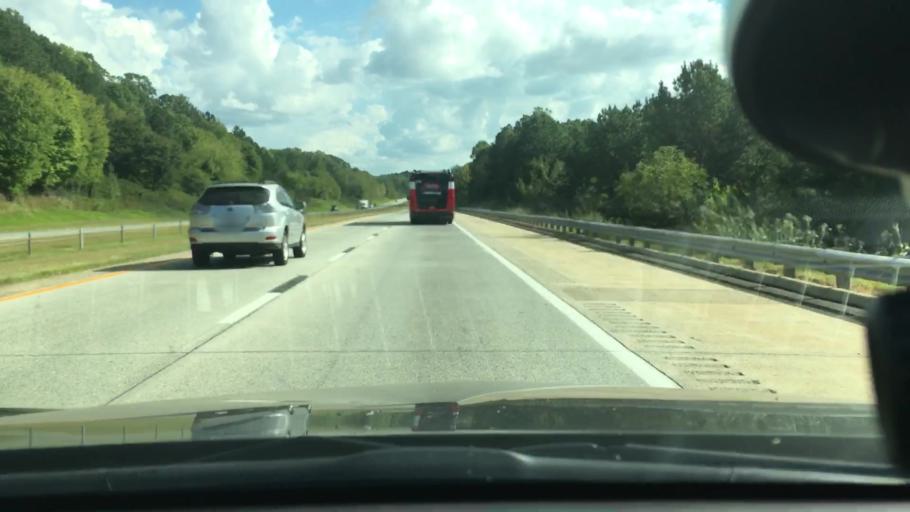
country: US
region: North Carolina
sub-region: Orange County
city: Hillsborough
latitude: 36.0035
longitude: -79.0805
